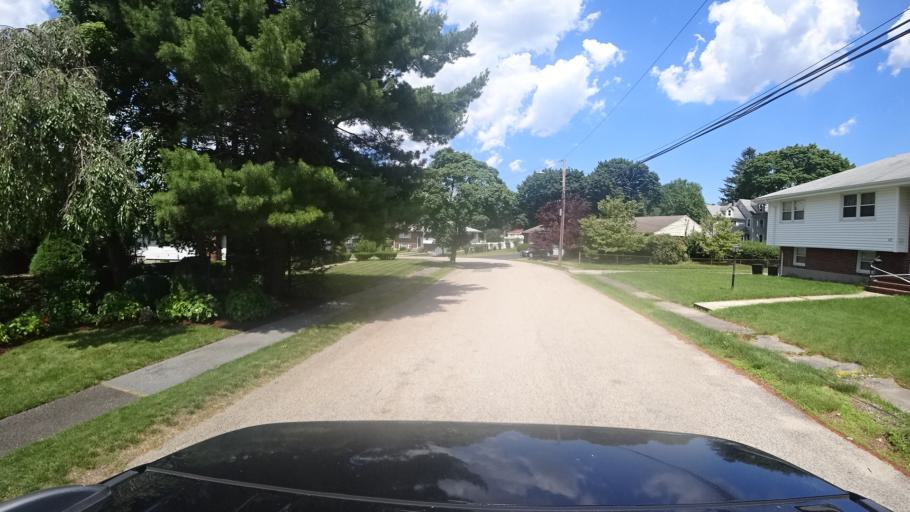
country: US
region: Massachusetts
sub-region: Norfolk County
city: Dedham
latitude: 42.2698
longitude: -71.1840
